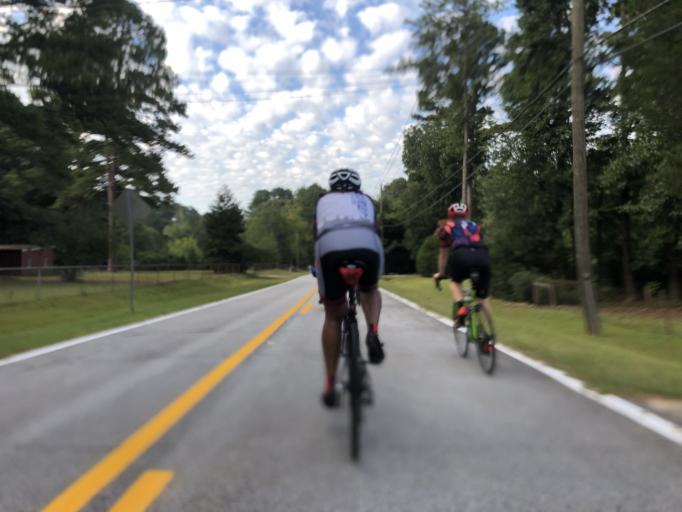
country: US
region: Georgia
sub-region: Fulton County
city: Fairburn
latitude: 33.6011
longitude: -84.6528
